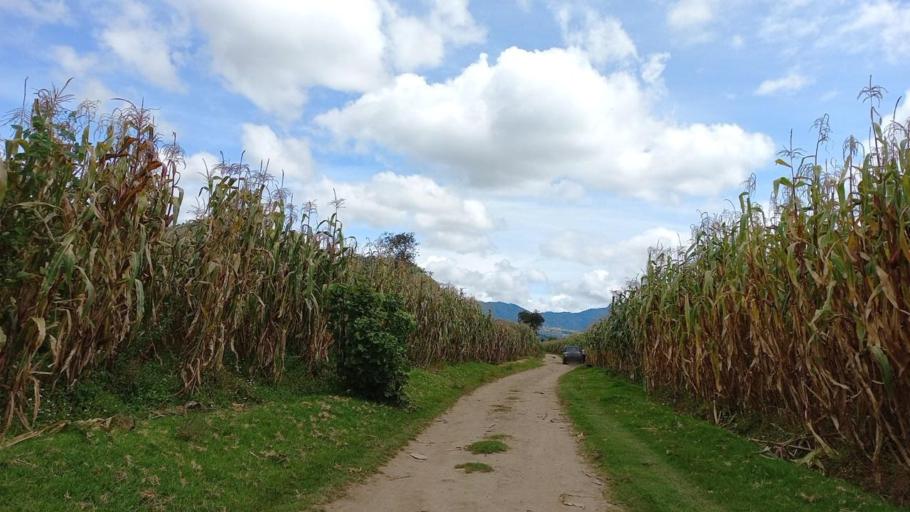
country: GT
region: Totonicapan
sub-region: Municipio de San Andres Xecul
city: San Andres Xecul
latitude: 14.8956
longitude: -91.4724
